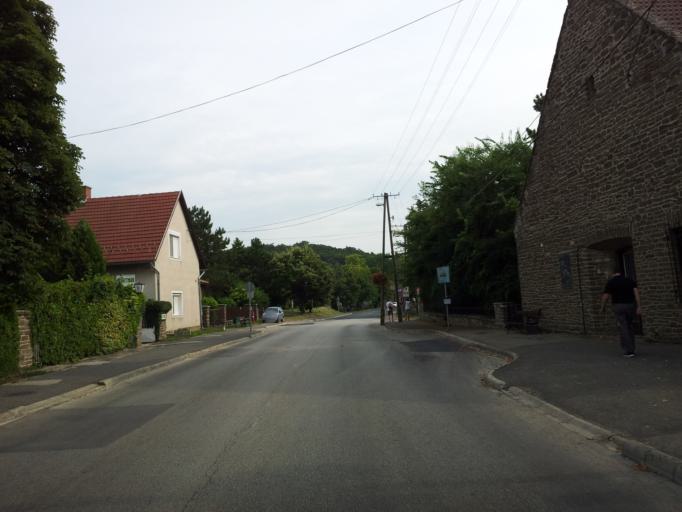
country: HU
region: Veszprem
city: Tihany
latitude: 46.9088
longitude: 17.8907
